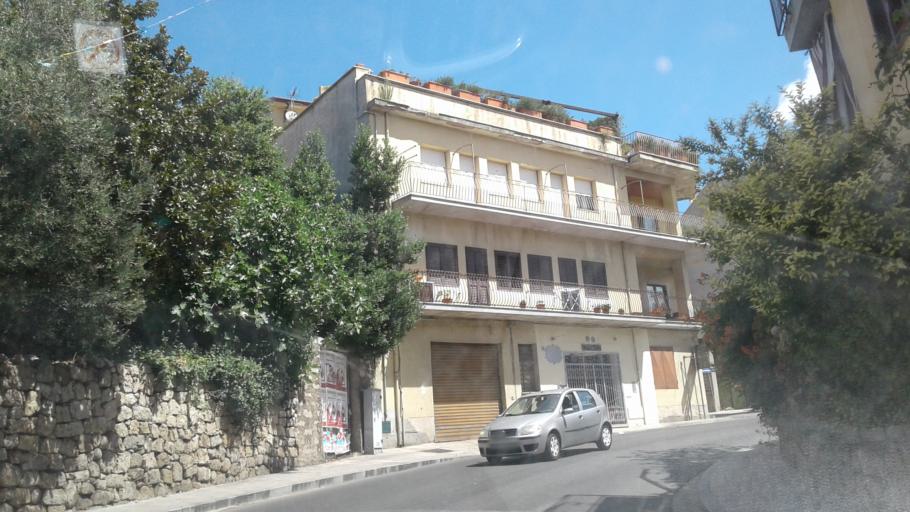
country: IT
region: Sardinia
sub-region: Provincia di Olbia-Tempio
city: Calangianus
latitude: 40.9210
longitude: 9.1928
